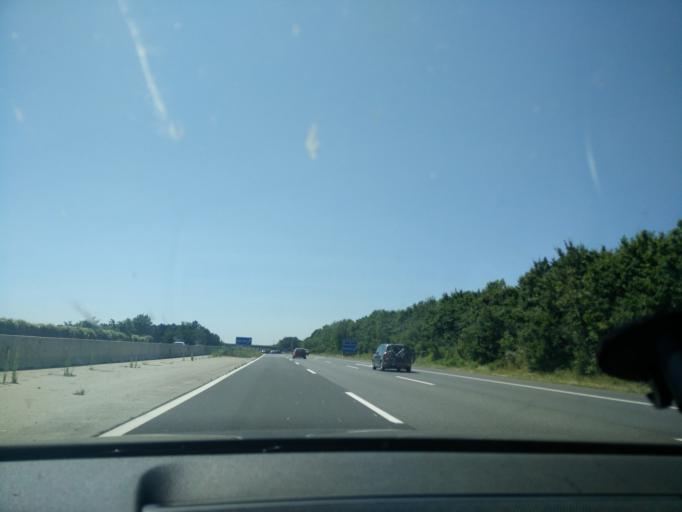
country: AT
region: Lower Austria
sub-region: Politischer Bezirk Baden
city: Leobersdorf
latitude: 47.9400
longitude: 16.2121
